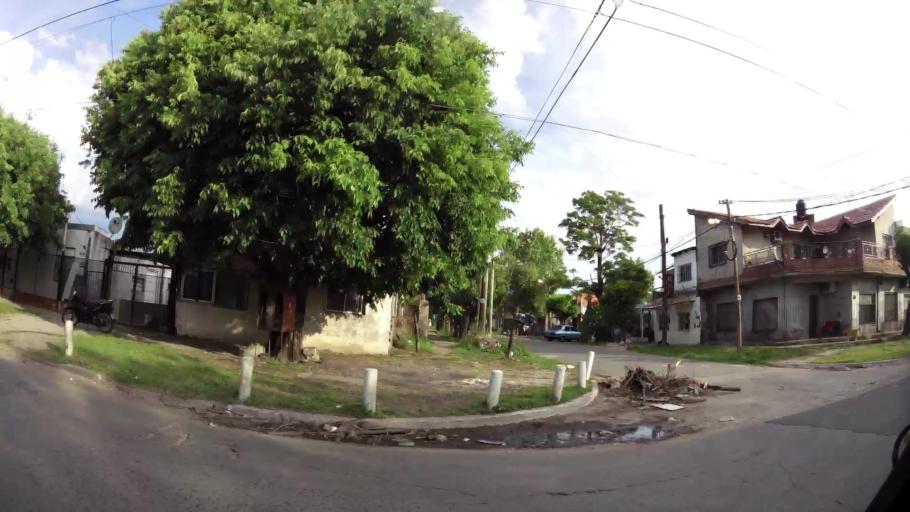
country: AR
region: Buenos Aires
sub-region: Partido de Quilmes
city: Quilmes
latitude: -34.7508
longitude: -58.2587
